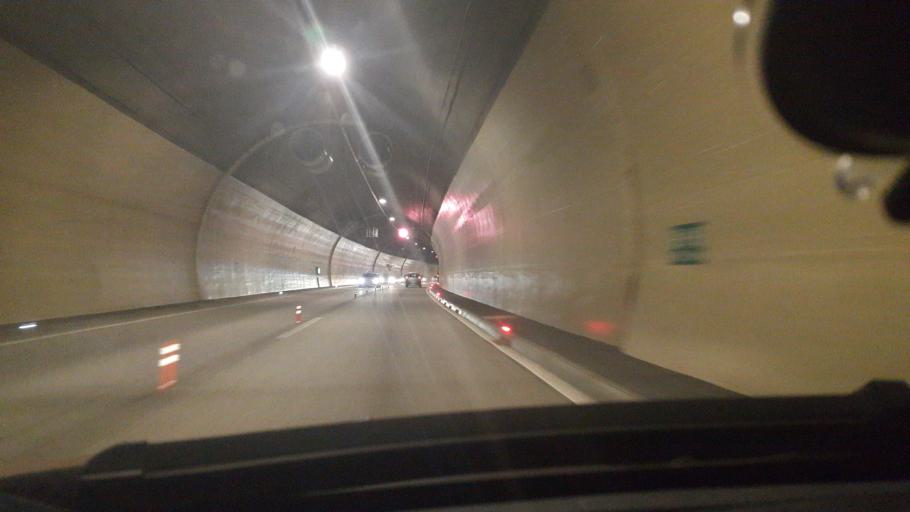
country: AT
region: Carinthia
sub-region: Klagenfurt am Woerthersee
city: Klagenfurt am Woerthersee
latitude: 46.6501
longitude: 14.3222
